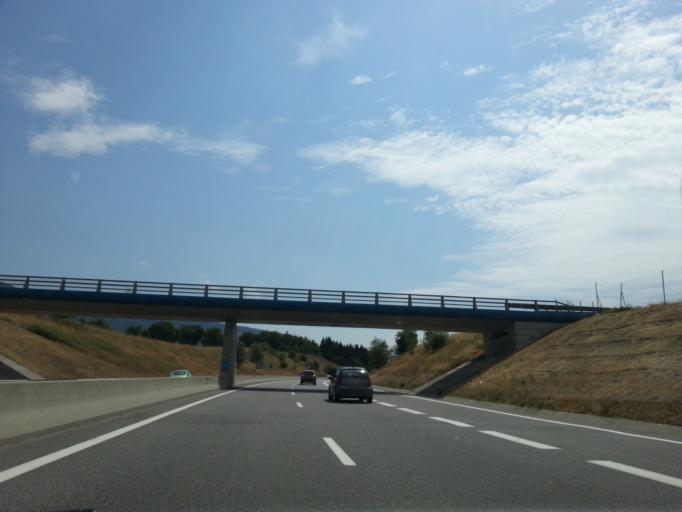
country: FR
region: Rhone-Alpes
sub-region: Departement de la Haute-Savoie
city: Feigeres
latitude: 46.1085
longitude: 6.0946
